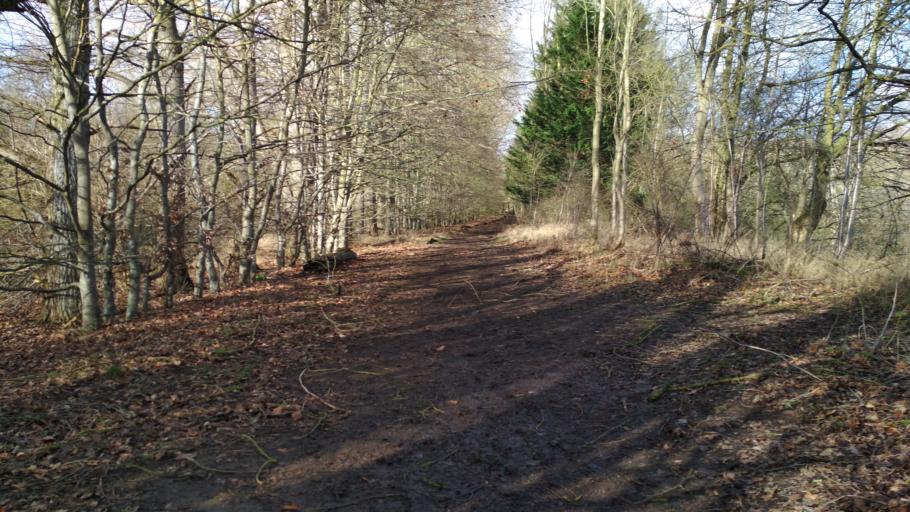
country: GB
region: England
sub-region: Oxfordshire
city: Radley
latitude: 51.6733
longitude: -1.2526
